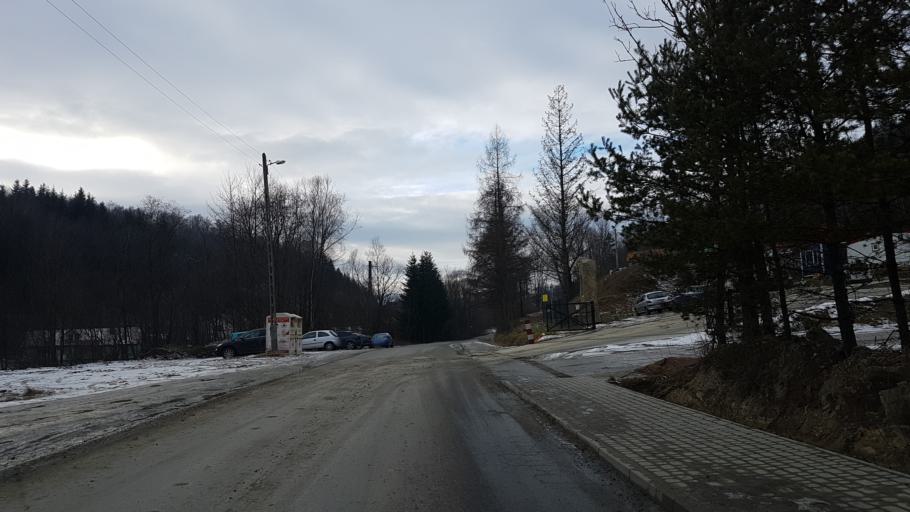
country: PL
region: Lesser Poland Voivodeship
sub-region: Powiat nowosadecki
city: Rytro
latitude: 49.5156
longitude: 20.6487
